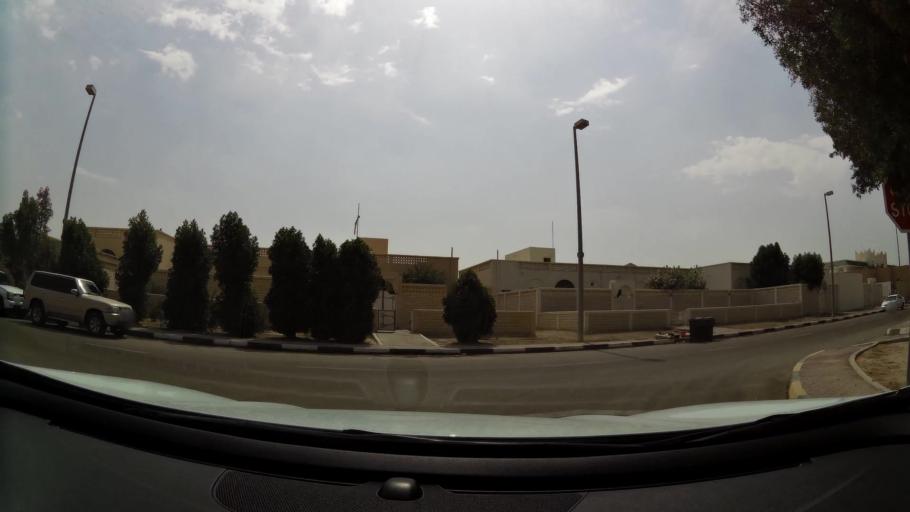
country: AE
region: Abu Dhabi
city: Abu Dhabi
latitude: 24.5299
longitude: 54.6842
